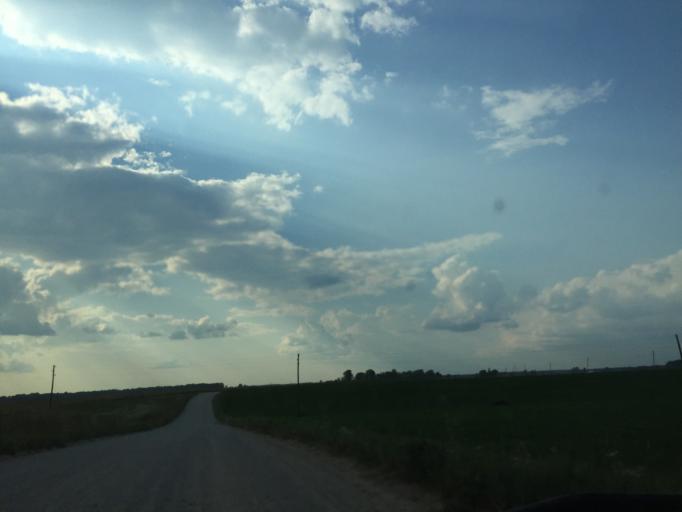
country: LT
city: Zagare
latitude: 56.4498
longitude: 23.1678
